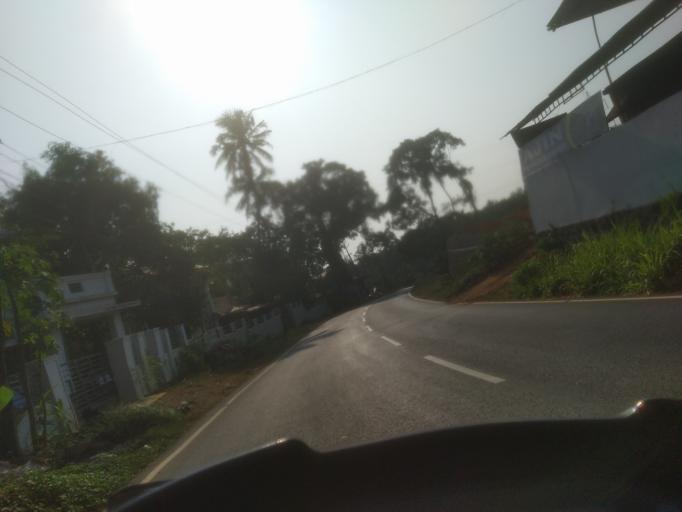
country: IN
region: Kerala
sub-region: Ernakulam
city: Piravam
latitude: 9.8306
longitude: 76.5075
